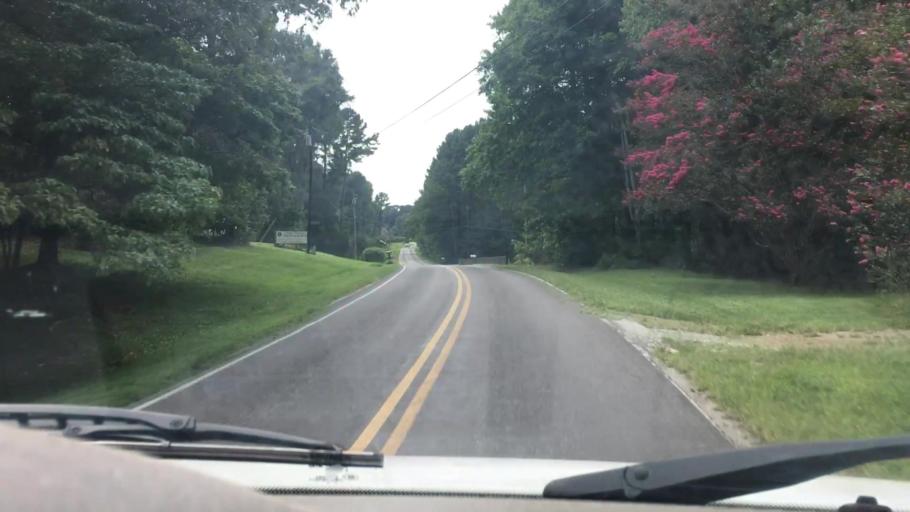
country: US
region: North Carolina
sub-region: Iredell County
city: Mooresville
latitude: 35.6627
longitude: -80.7985
